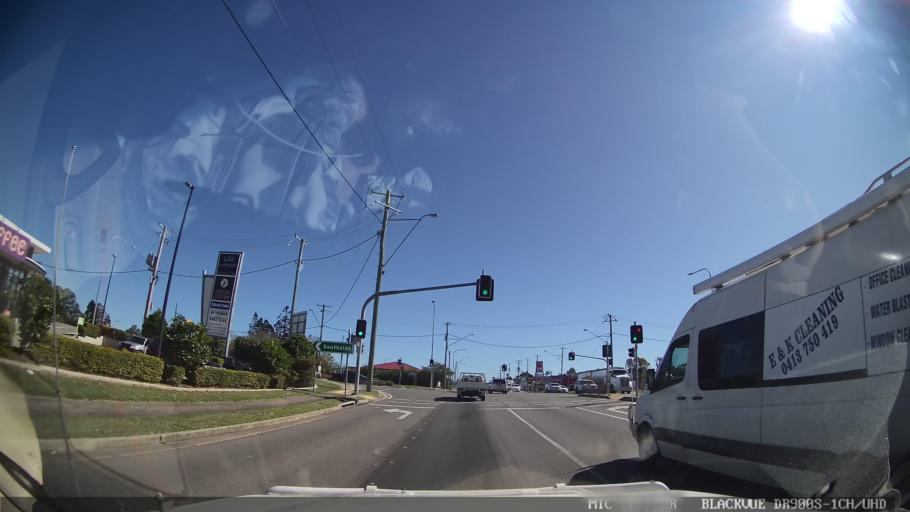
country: AU
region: Queensland
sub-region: Gympie Regional Council
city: Gympie
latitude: -26.1926
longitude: 152.6584
